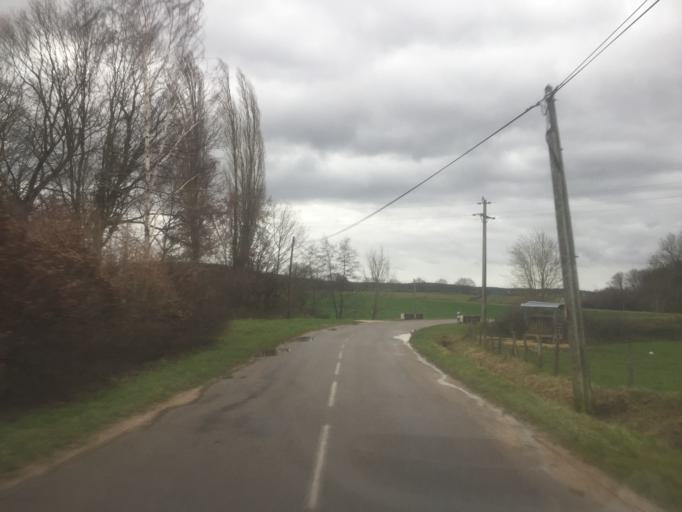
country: FR
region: Franche-Comte
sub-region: Departement de la Haute-Saone
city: Pesmes
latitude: 47.2226
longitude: 5.5023
